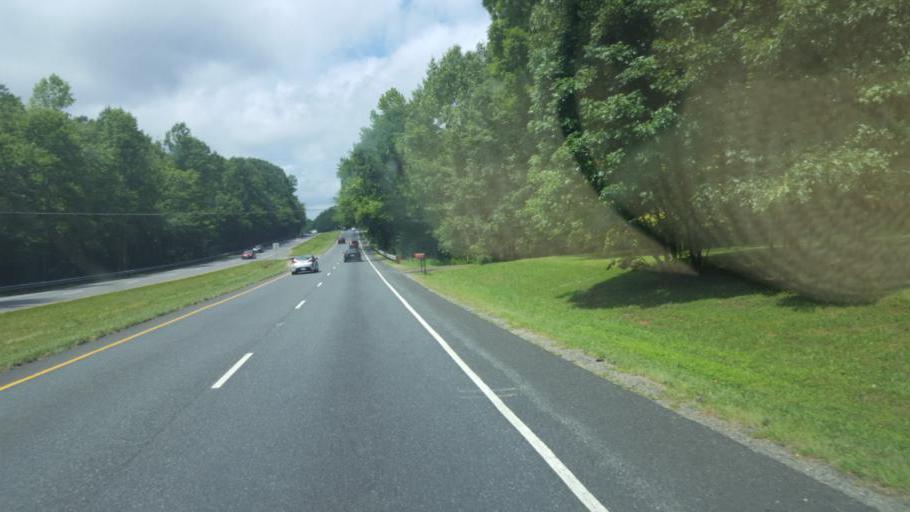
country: US
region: Virginia
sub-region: Stafford County
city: Falmouth
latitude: 38.4036
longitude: -77.5761
